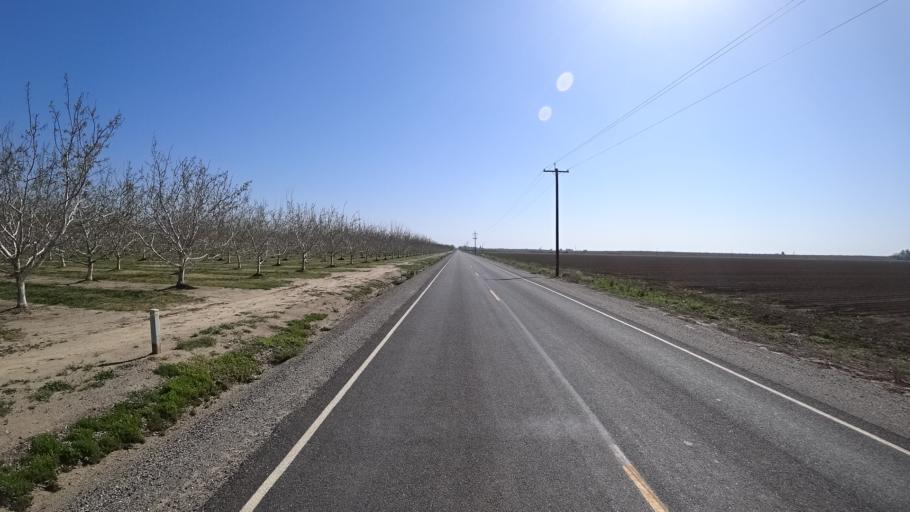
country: US
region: California
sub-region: Glenn County
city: Hamilton City
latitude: 39.6597
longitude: -122.0448
